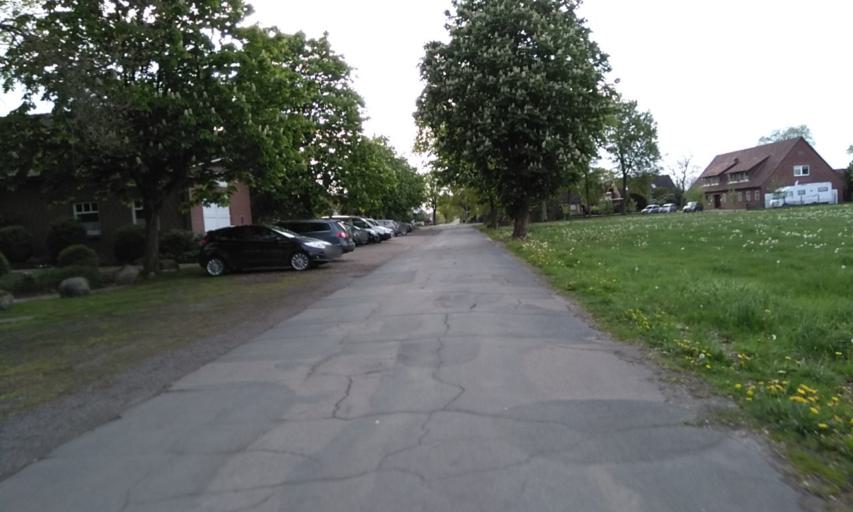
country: DE
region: Lower Saxony
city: Ahlerstedt
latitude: 53.3958
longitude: 9.4898
